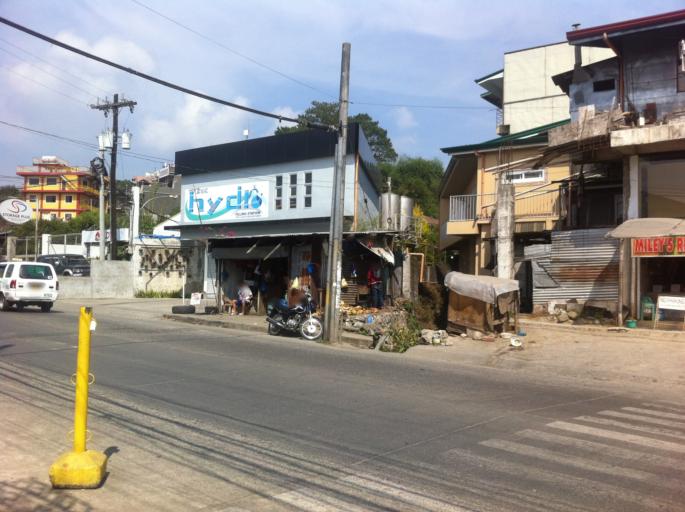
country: PH
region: Cordillera
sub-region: Province of Benguet
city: La Trinidad
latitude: 16.4589
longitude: 120.5793
